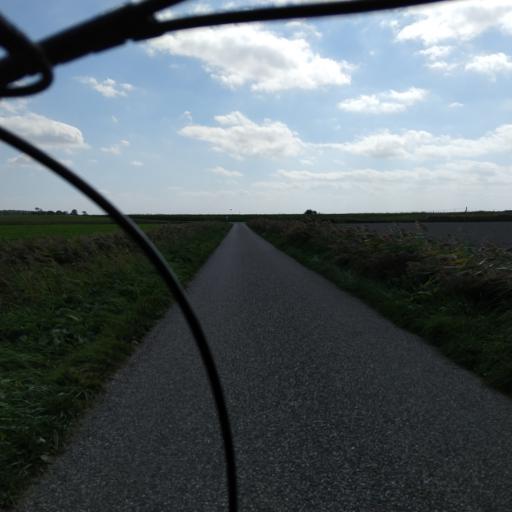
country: NL
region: Zeeland
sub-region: Gemeente Noord-Beveland
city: Kamperland
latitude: 51.5915
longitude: 3.7630
